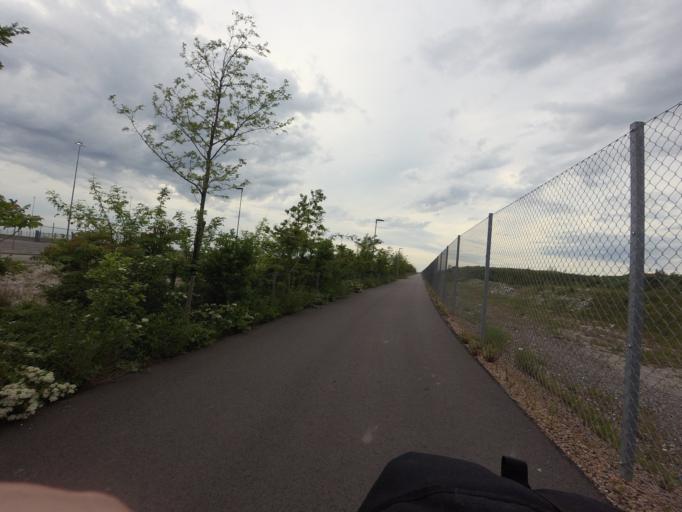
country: SE
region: Skane
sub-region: Malmo
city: Malmoe
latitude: 55.6318
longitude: 13.0070
